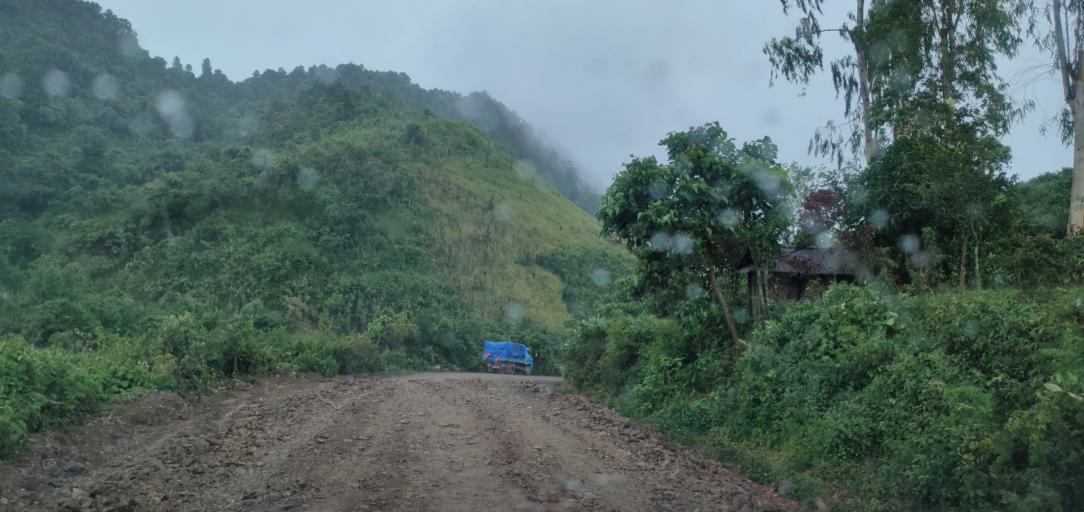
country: LA
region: Phongsali
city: Phongsali
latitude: 21.4307
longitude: 102.1605
